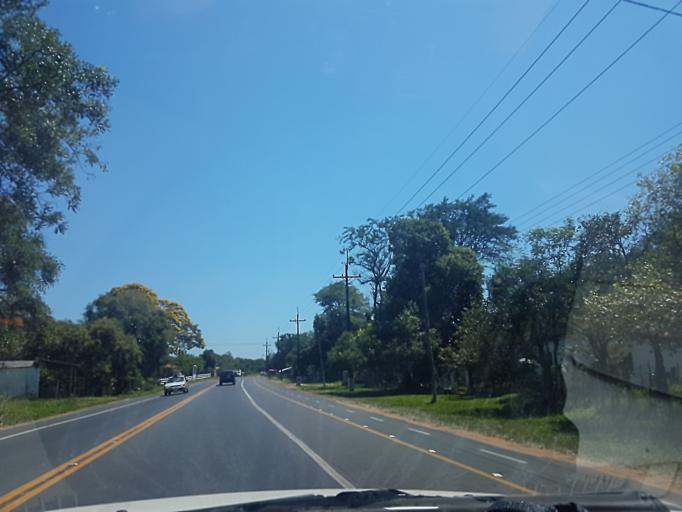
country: PY
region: Central
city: Aregua
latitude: -25.2342
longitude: -57.4205
